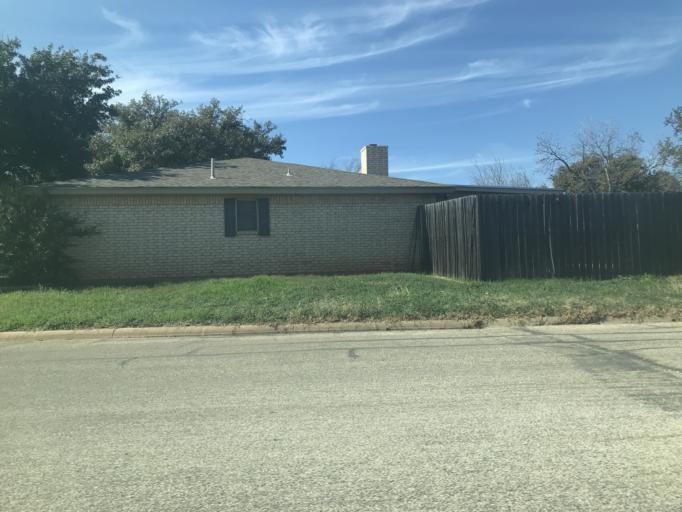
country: US
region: Texas
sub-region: Tom Green County
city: San Angelo
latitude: 31.4285
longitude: -100.4895
